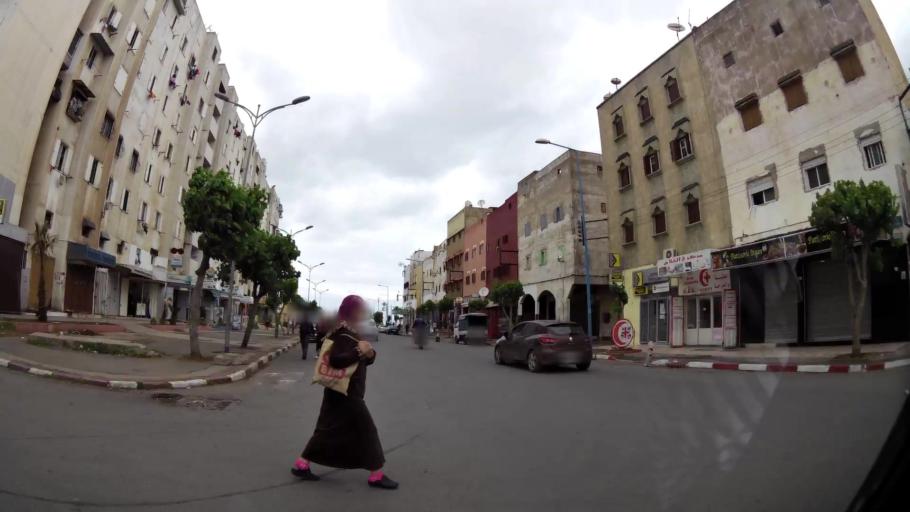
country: MA
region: Grand Casablanca
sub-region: Casablanca
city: Casablanca
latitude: 33.5871
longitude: -7.5515
